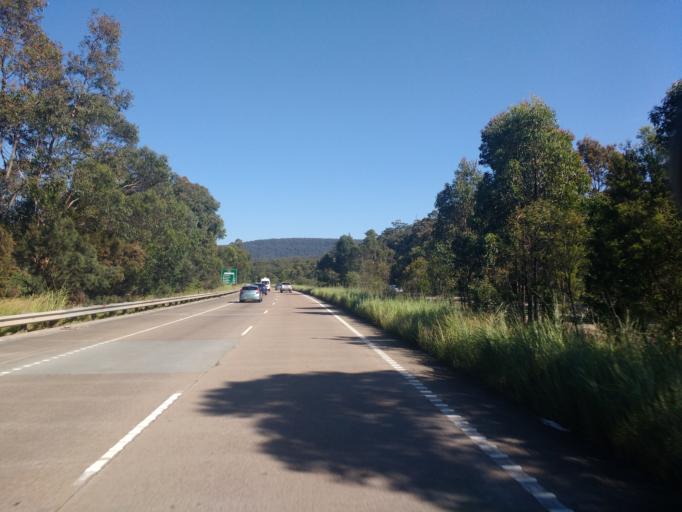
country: AU
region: New South Wales
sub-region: Lake Macquarie Shire
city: Holmesville
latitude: -32.8956
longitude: 151.5776
